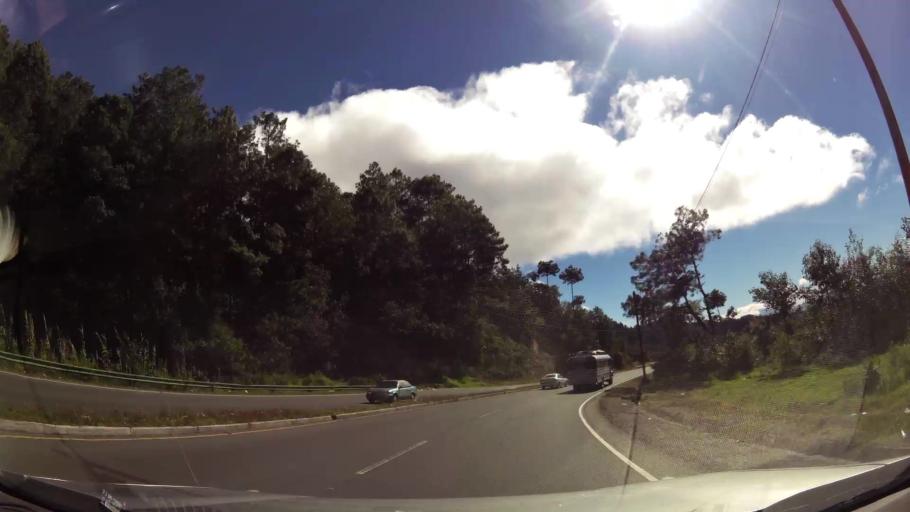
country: GT
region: Solola
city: Concepcion
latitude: 14.8378
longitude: -91.1797
